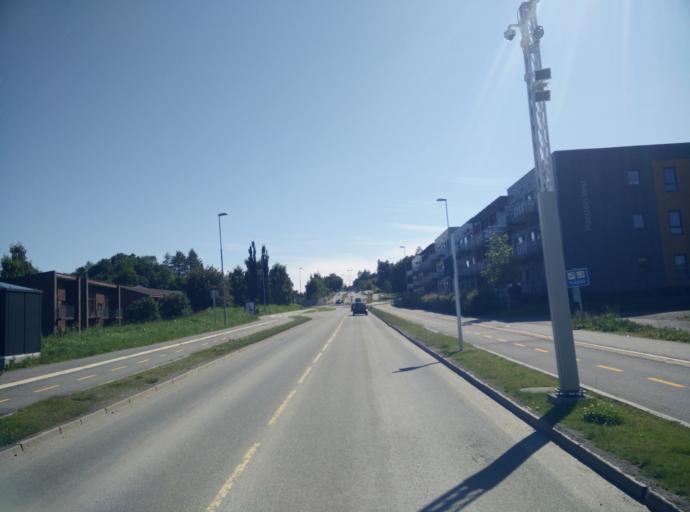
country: NO
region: Sor-Trondelag
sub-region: Trondheim
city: Trondheim
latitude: 63.4052
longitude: 10.3588
